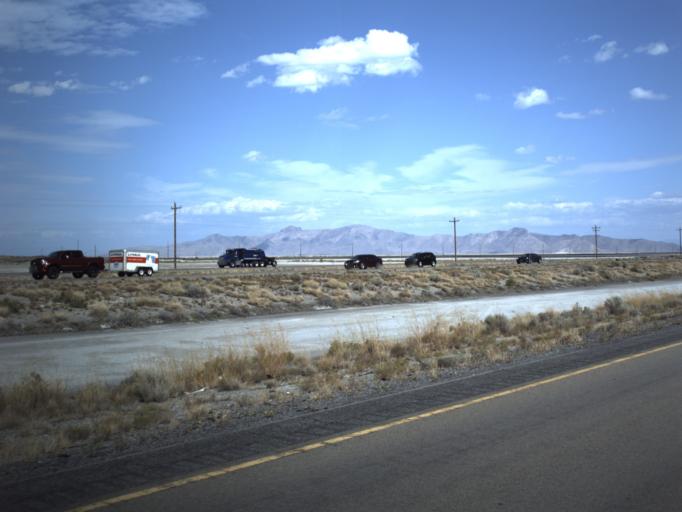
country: US
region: Utah
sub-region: Tooele County
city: Grantsville
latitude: 40.7530
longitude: -112.7264
